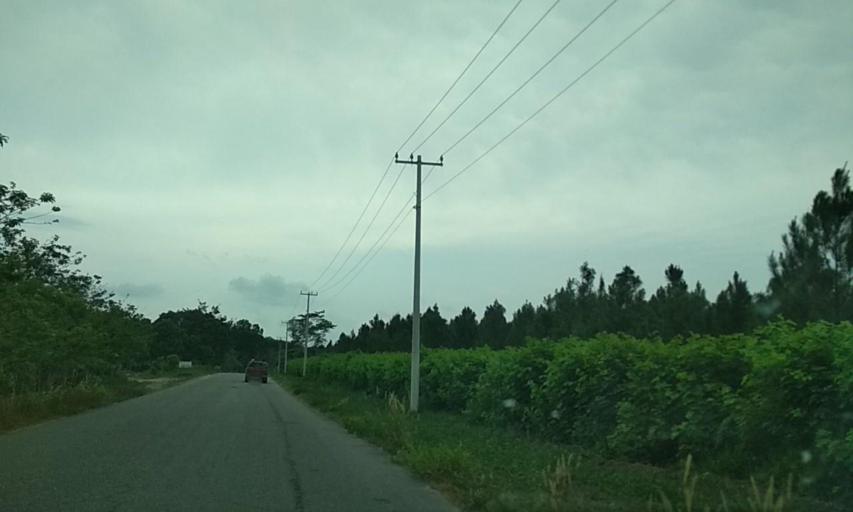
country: MX
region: Veracruz
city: Las Choapas
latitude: 17.8467
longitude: -94.1052
